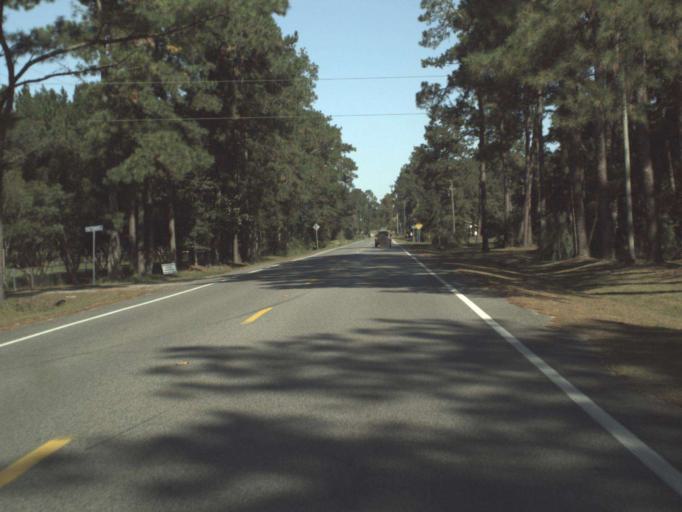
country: US
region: Florida
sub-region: Jefferson County
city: Monticello
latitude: 30.3518
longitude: -83.9904
